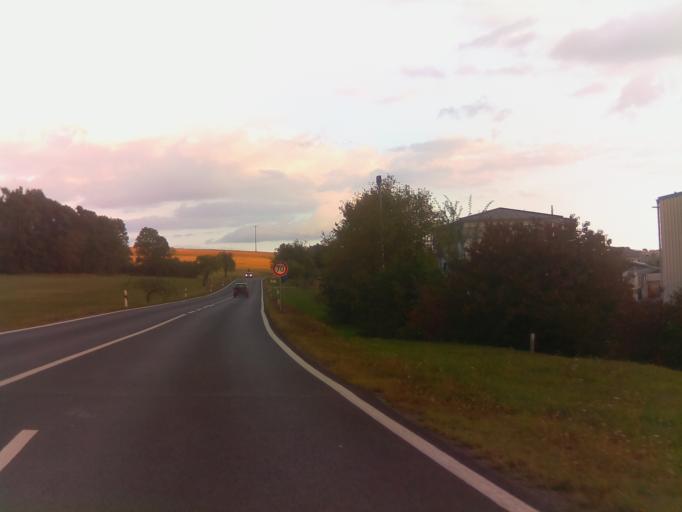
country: DE
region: Bavaria
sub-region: Regierungsbezirk Unterfranken
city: Oberleichtersbach
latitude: 50.2873
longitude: 9.7914
